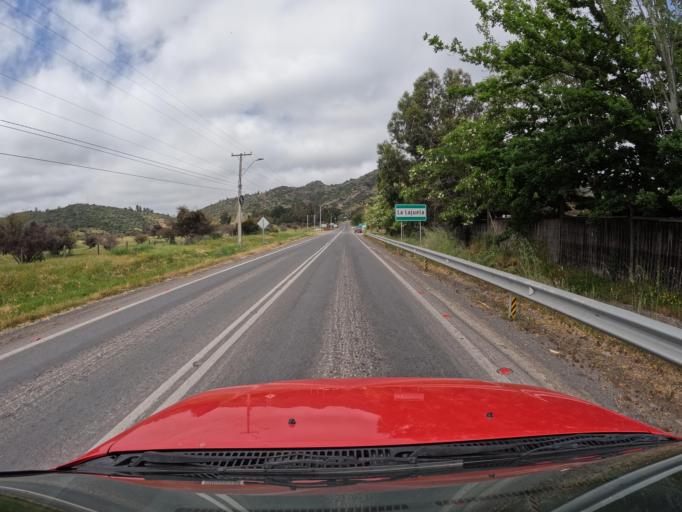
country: CL
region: O'Higgins
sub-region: Provincia de Colchagua
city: Santa Cruz
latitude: -34.6578
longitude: -71.4103
